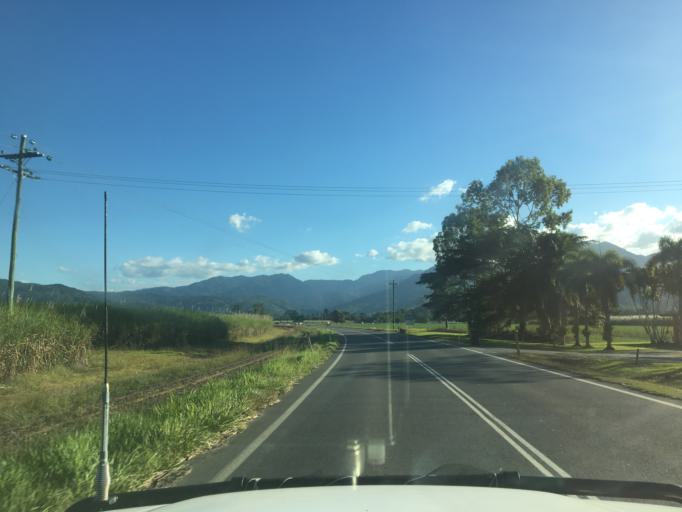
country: AU
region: Queensland
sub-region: Cairns
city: Port Douglas
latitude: -16.4793
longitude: 145.3940
